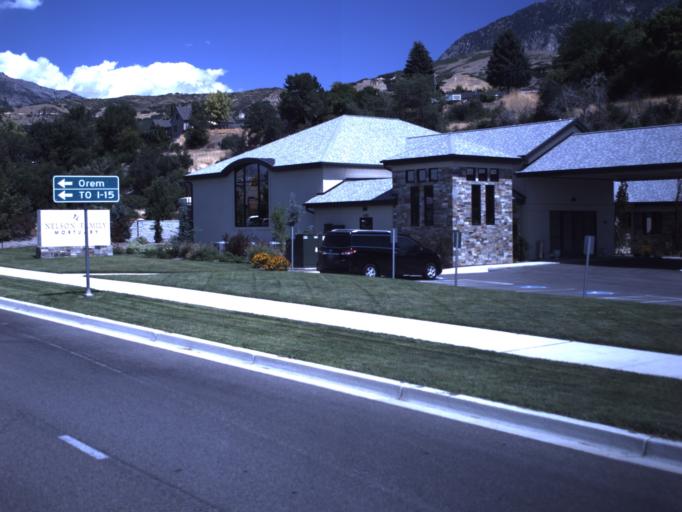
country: US
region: Utah
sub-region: Utah County
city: Orem
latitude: 40.2969
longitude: -111.6570
